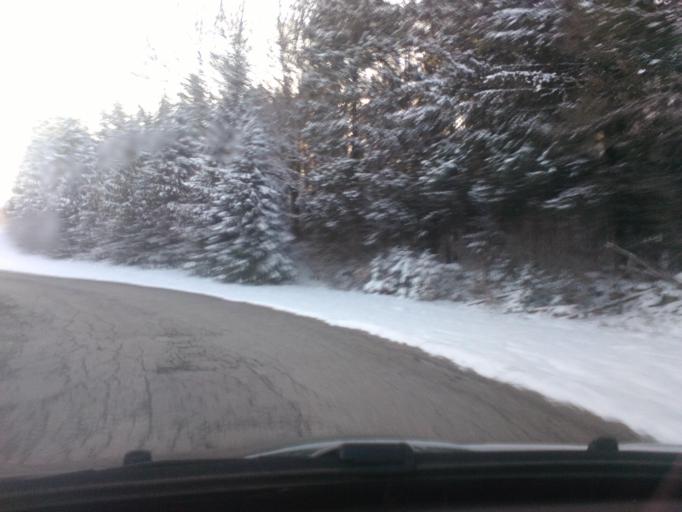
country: FR
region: Lorraine
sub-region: Departement des Vosges
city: Granges-sur-Vologne
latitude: 48.1390
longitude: 6.8318
